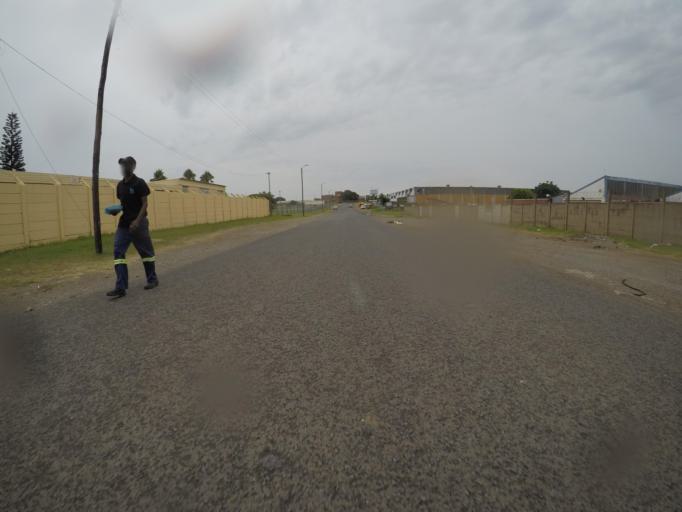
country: ZA
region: Eastern Cape
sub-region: Buffalo City Metropolitan Municipality
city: East London
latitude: -32.9748
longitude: 27.8227
